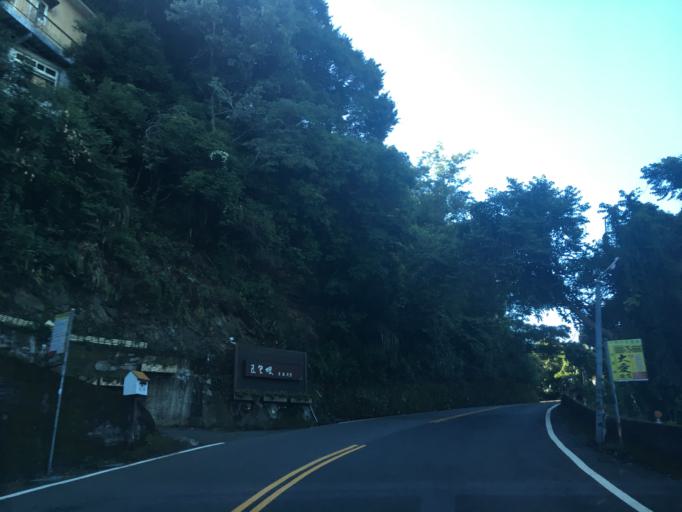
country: TW
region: Taiwan
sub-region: Nantou
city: Puli
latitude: 24.0346
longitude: 121.1493
